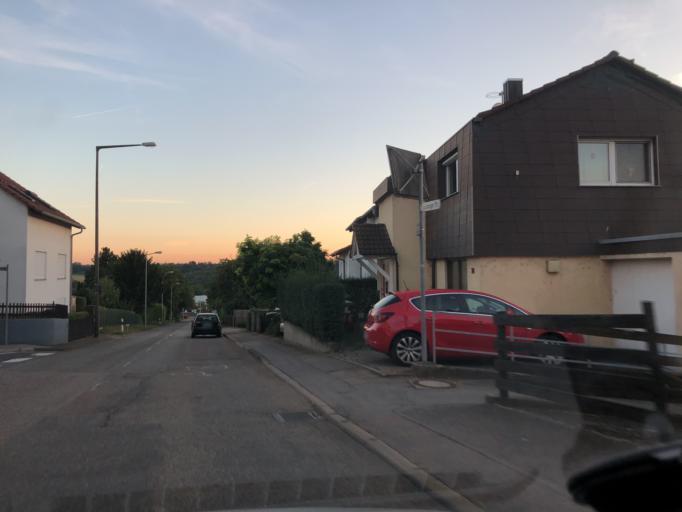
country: DE
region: Baden-Wuerttemberg
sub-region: Regierungsbezirk Stuttgart
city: Marbach am Neckar
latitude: 48.9048
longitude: 9.2648
